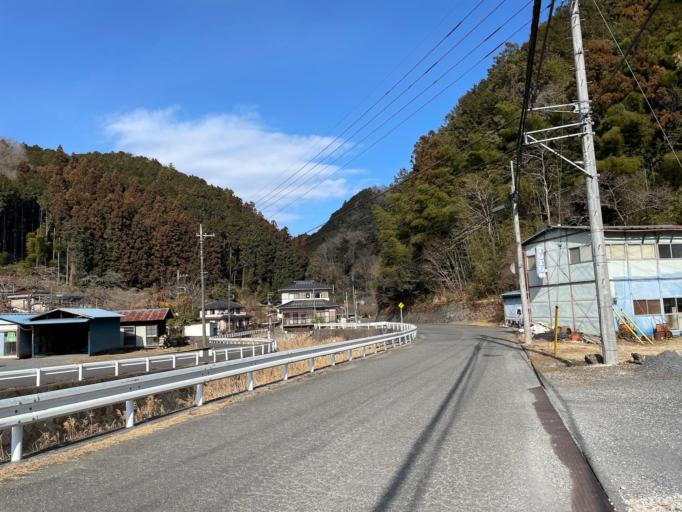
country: JP
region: Saitama
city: Hanno
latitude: 35.8443
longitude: 139.2573
